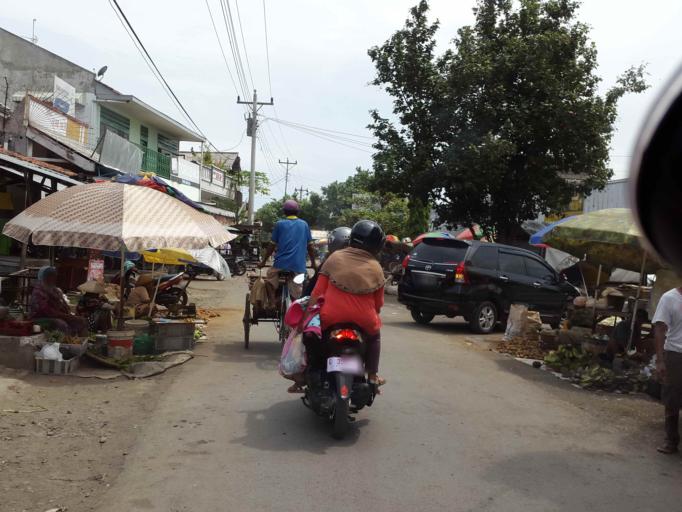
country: ID
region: Central Java
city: Pemalang
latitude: -6.8892
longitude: 109.3905
